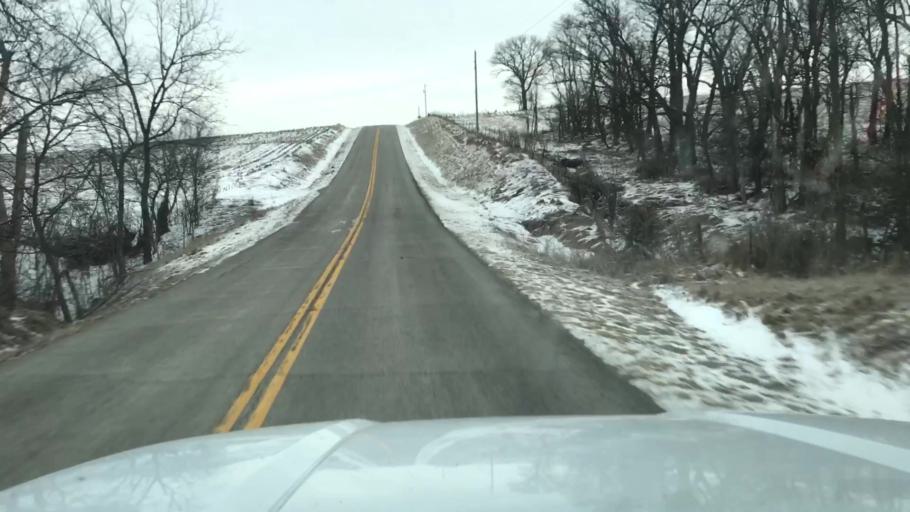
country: US
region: Missouri
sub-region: Holt County
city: Oregon
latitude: 40.0916
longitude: -94.9744
